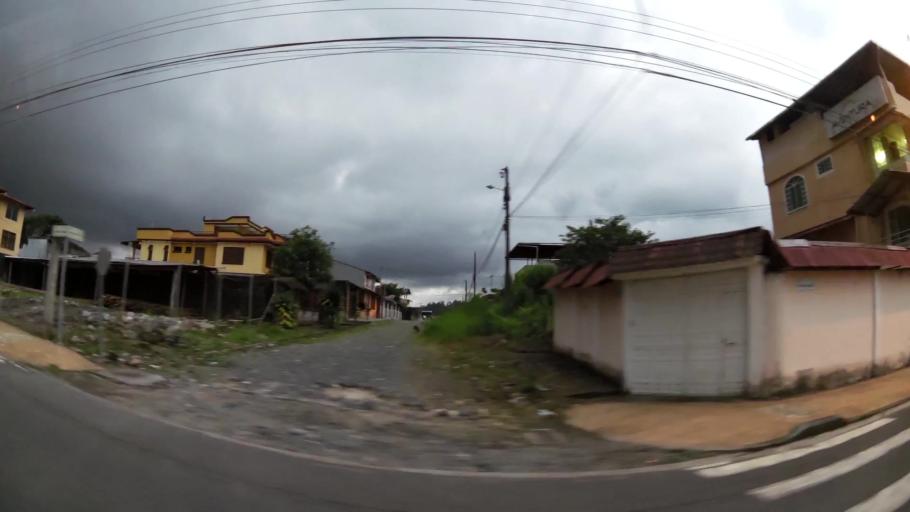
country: EC
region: Pastaza
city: Puyo
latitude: -1.4827
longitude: -78.0072
